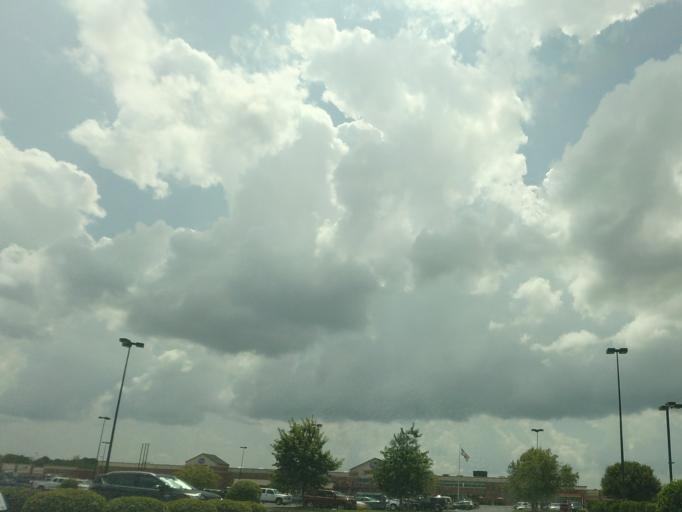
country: US
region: Georgia
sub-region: Houston County
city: Centerville
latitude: 32.5541
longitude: -83.6601
